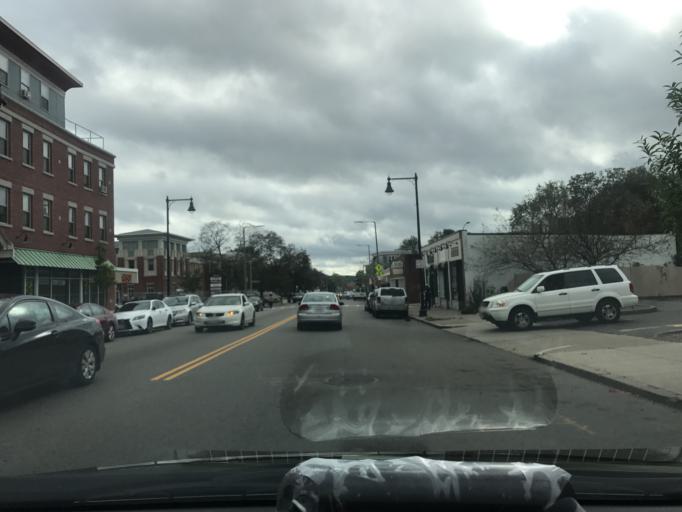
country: US
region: Massachusetts
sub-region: Suffolk County
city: South Boston
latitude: 42.2952
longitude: -71.0721
